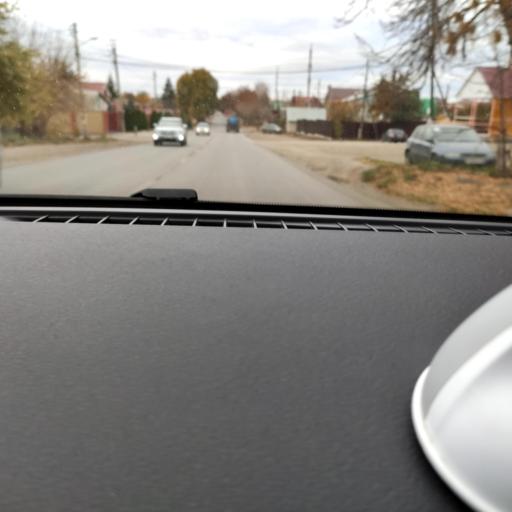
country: RU
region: Samara
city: Samara
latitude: 53.1773
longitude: 50.1841
